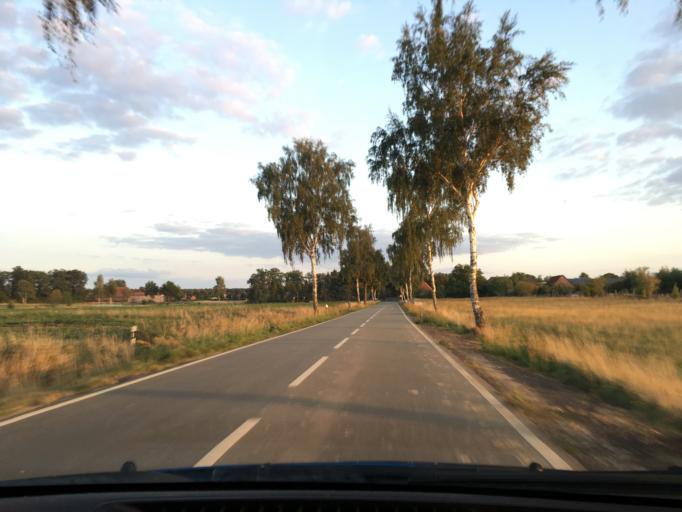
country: DE
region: Lower Saxony
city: Nahrendorf
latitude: 53.1624
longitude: 10.8097
